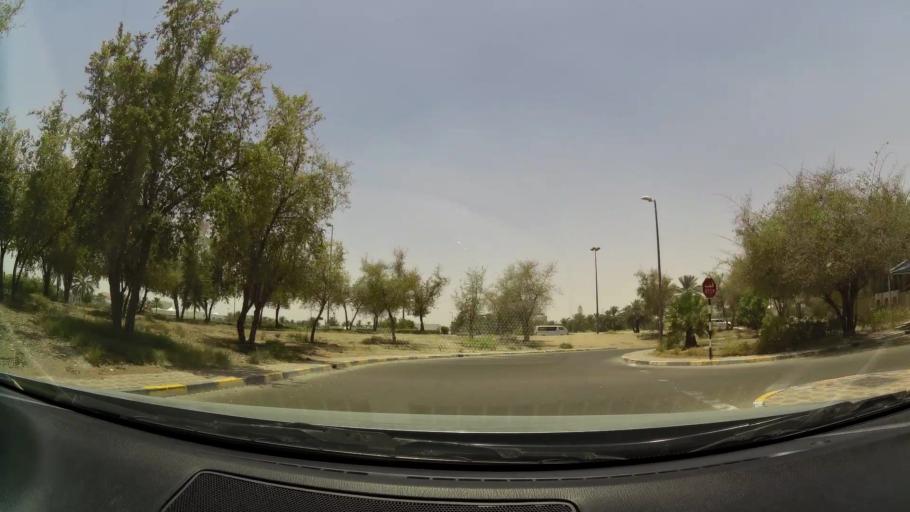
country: OM
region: Al Buraimi
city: Al Buraymi
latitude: 24.2596
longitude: 55.7210
